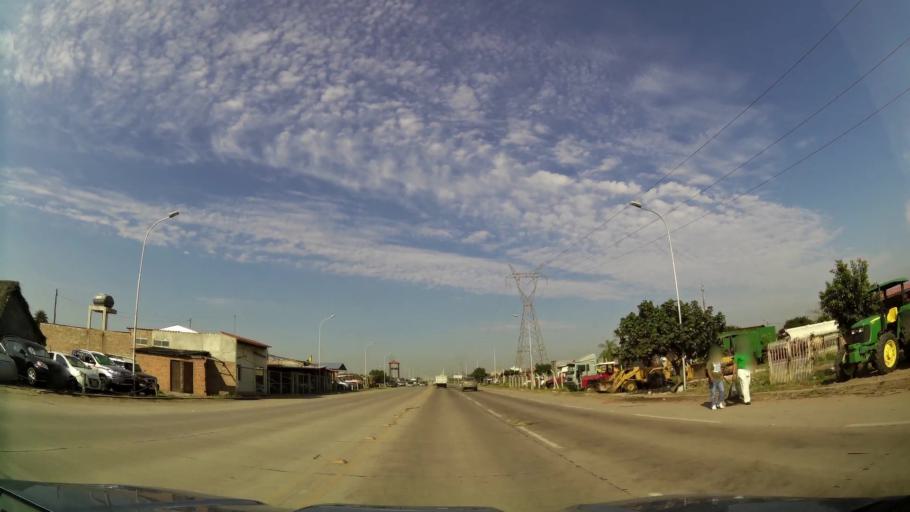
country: BO
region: Santa Cruz
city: Santa Cruz de la Sierra
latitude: -17.7263
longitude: -63.1351
